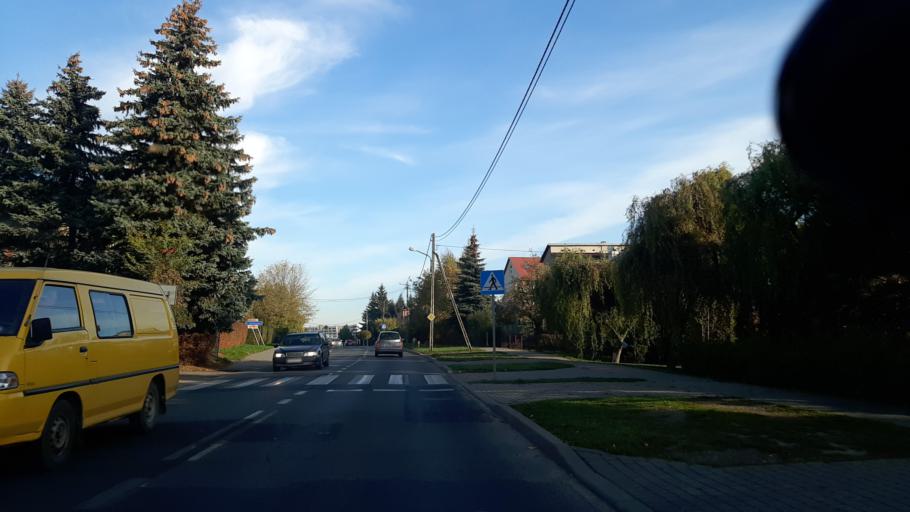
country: PL
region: Lublin Voivodeship
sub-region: Powiat lubelski
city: Lublin
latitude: 51.2653
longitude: 22.5815
